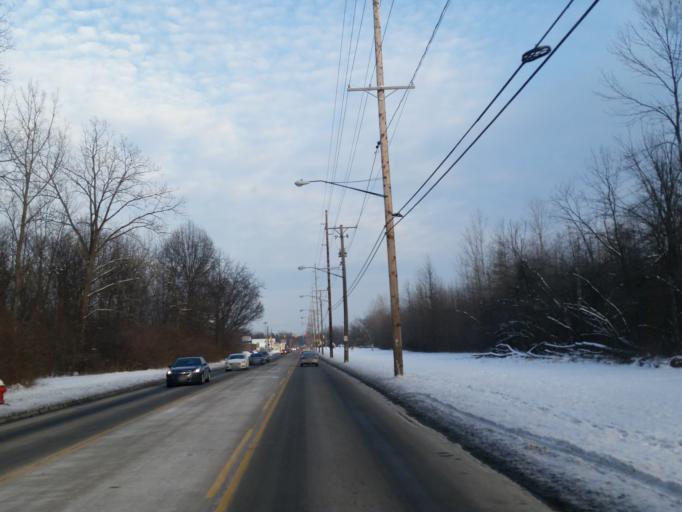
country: US
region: Ohio
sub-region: Lorain County
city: Lorain
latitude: 41.4654
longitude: -82.1497
